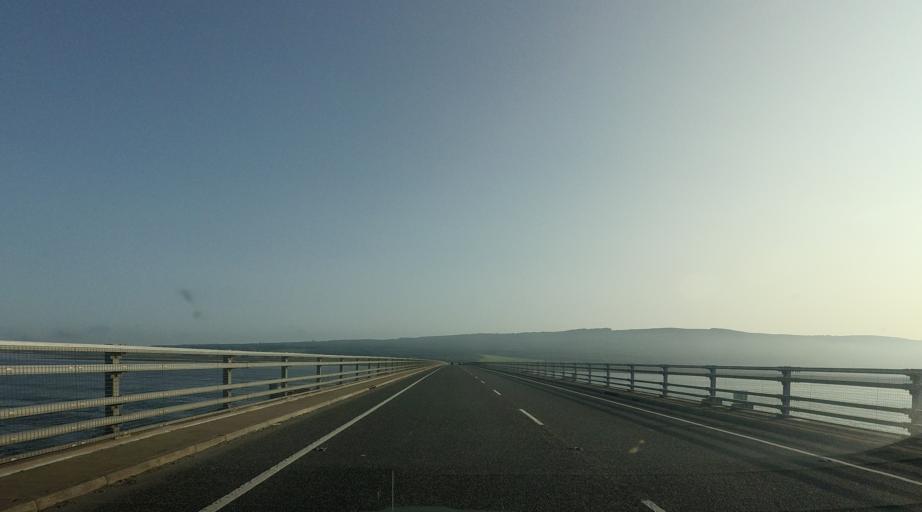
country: GB
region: Scotland
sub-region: Highland
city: Tain
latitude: 57.8454
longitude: -4.1109
